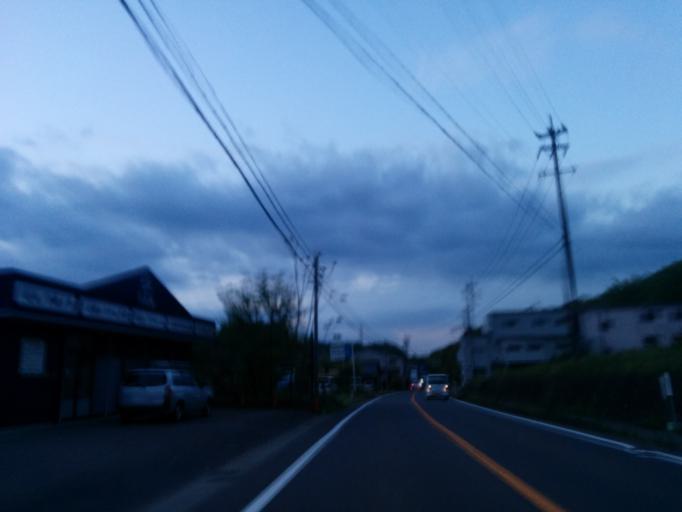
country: JP
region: Gifu
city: Kakamigahara
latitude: 35.4607
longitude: 136.8905
